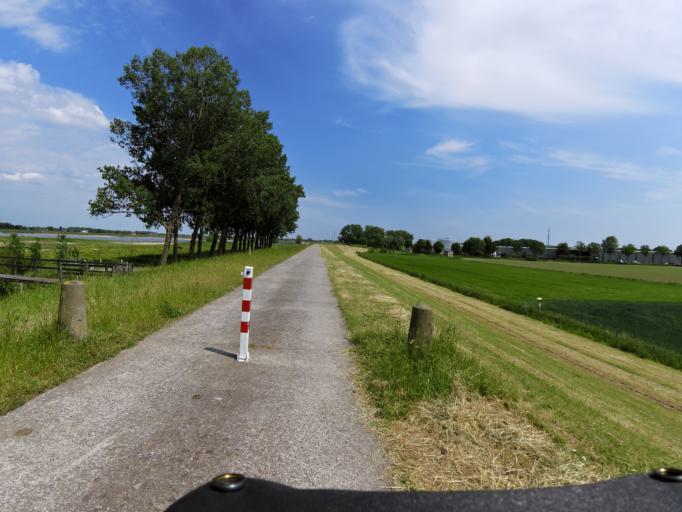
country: NL
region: North Brabant
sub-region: Gemeente Woudrichem
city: Woudrichem
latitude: 51.8204
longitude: 5.0740
